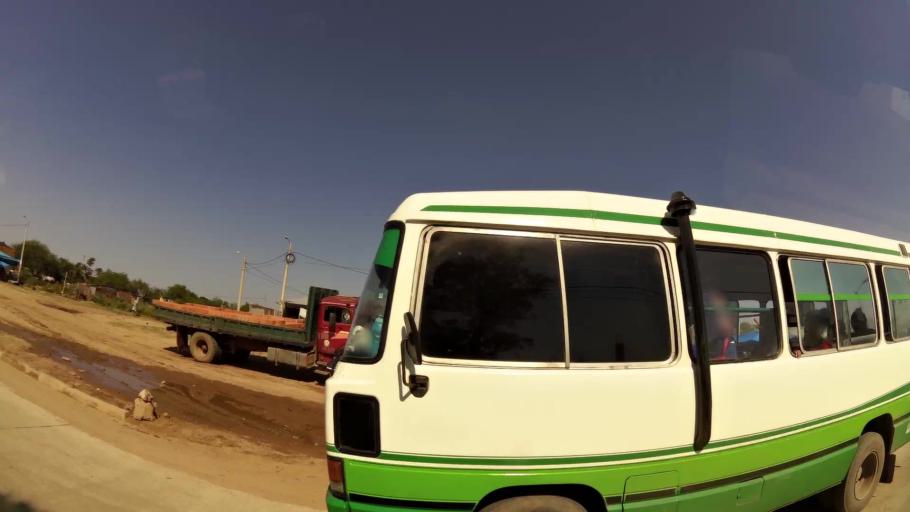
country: BO
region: Santa Cruz
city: Cotoca
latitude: -17.7271
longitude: -63.0877
